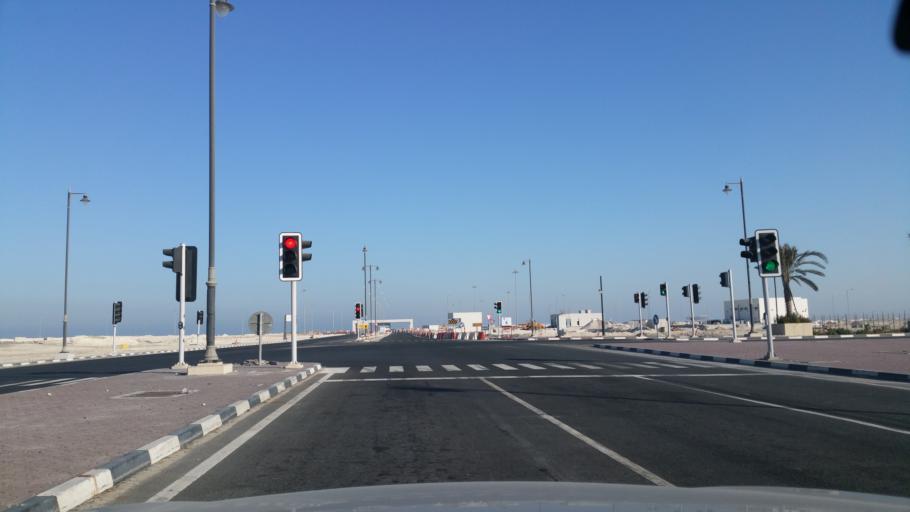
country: QA
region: Al Wakrah
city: Umm Sa'id
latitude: 25.0550
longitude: 51.6014
